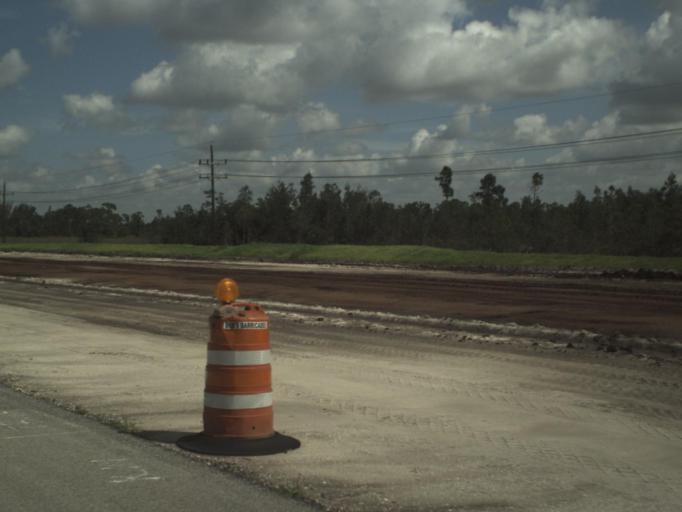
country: US
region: Florida
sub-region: Palm Beach County
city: Limestone Creek
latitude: 26.9230
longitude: -80.3218
